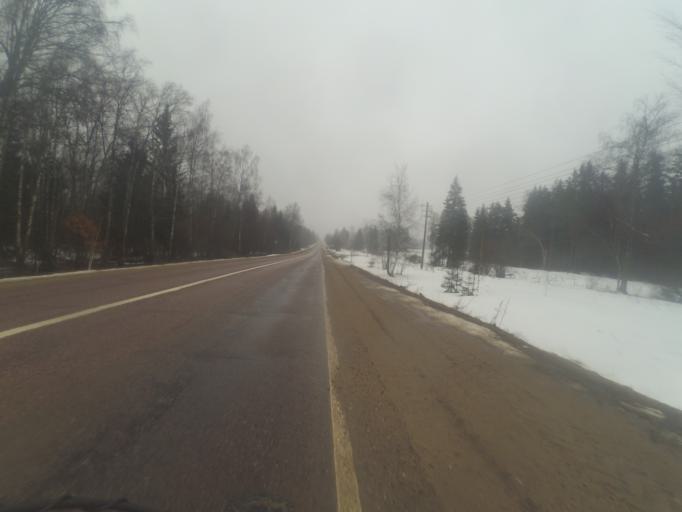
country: RU
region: Moskovskaya
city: Avtopoligon
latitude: 56.2621
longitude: 37.2776
